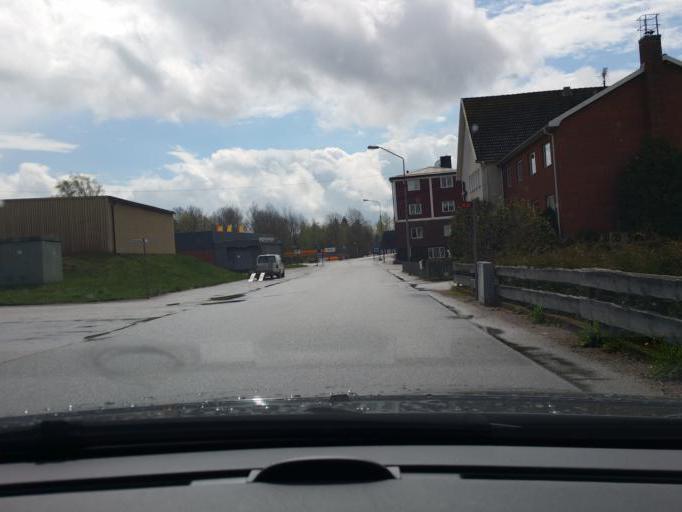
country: SE
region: Kronoberg
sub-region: Vaxjo Kommun
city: Lammhult
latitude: 57.1709
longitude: 14.5792
